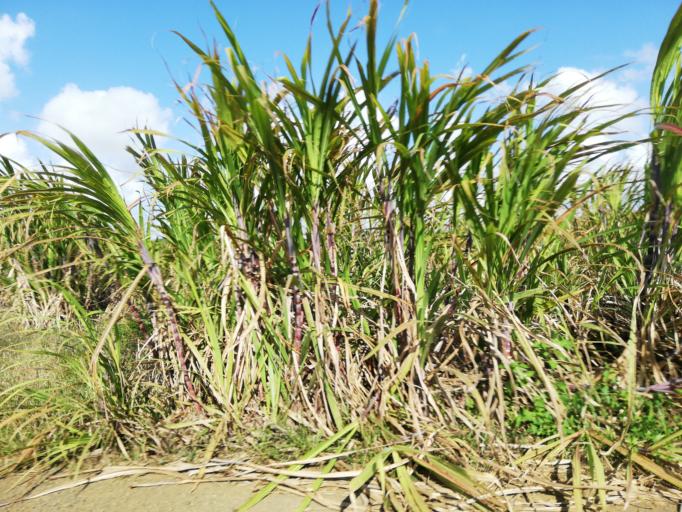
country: MU
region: Moka
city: Verdun
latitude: -20.2256
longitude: 57.5504
